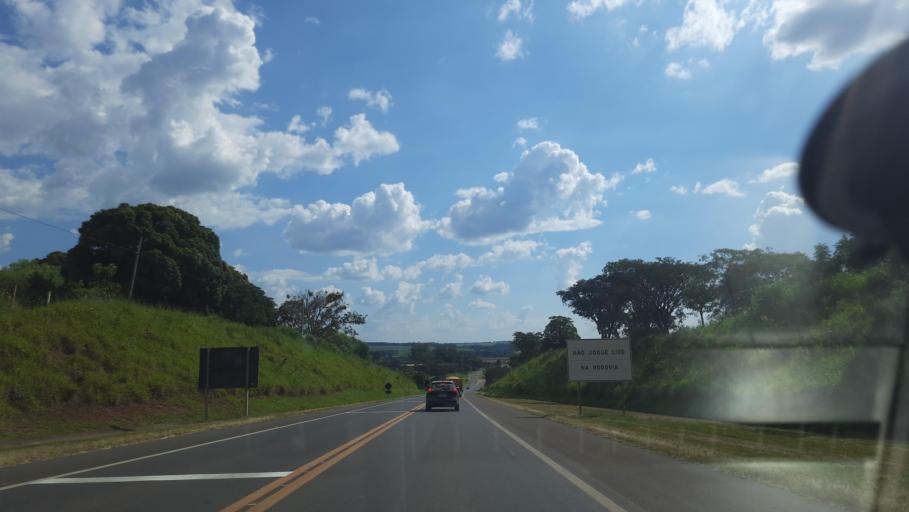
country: BR
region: Sao Paulo
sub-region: Casa Branca
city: Casa Branca
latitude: -21.7383
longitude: -46.9749
